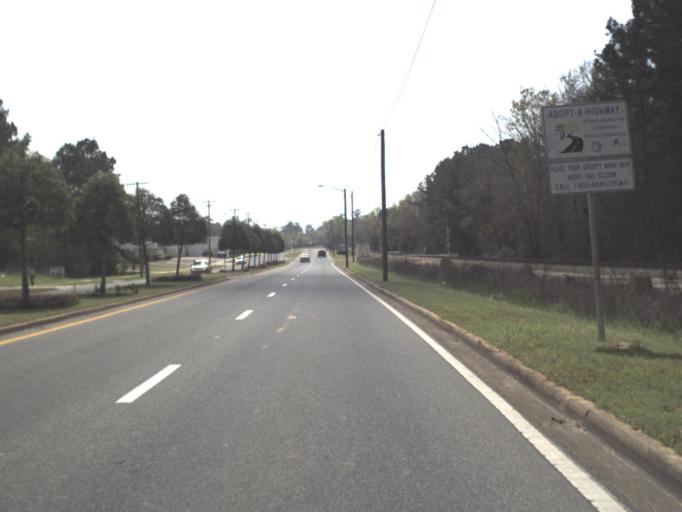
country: US
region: Florida
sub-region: Gadsden County
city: Havana
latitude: 30.6347
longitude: -84.4171
